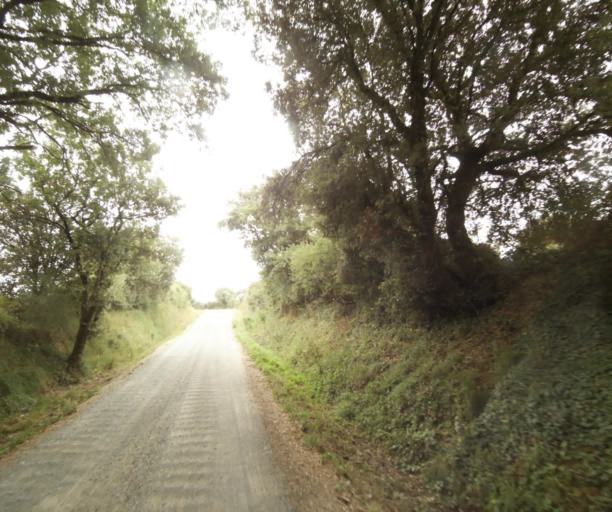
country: FR
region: Pays de la Loire
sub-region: Departement de la Vendee
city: Chateau-d'Olonne
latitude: 46.4976
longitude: -1.7394
